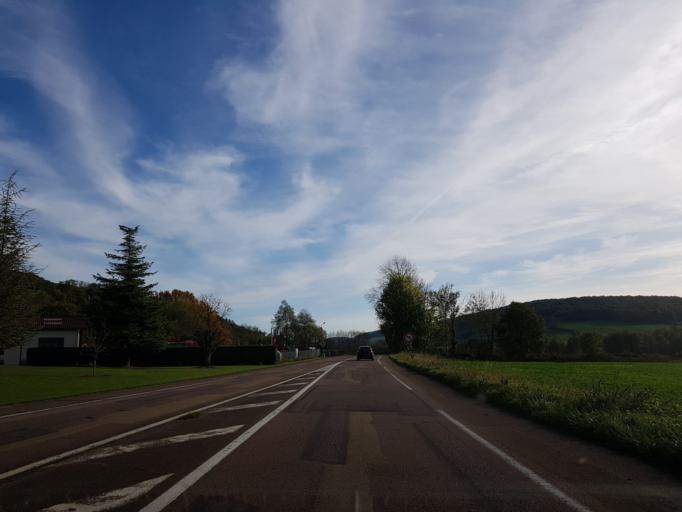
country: FR
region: Bourgogne
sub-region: Departement de la Cote-d'Or
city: Vitteaux
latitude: 47.3687
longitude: 4.5649
